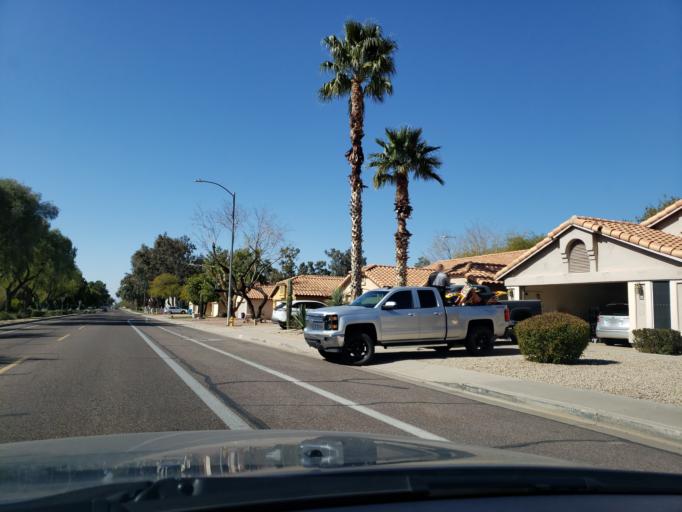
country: US
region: Arizona
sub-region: Maricopa County
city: Paradise Valley
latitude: 33.6476
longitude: -112.0554
